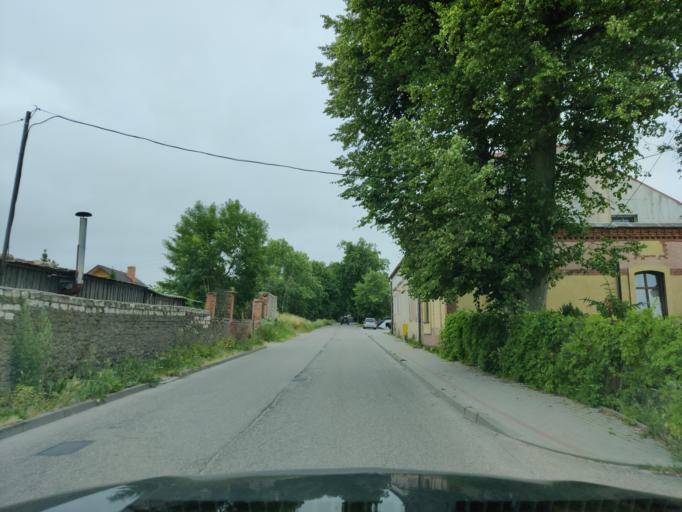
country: PL
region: Warmian-Masurian Voivodeship
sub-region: Powiat gizycki
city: Ryn
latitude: 53.9333
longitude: 21.5496
